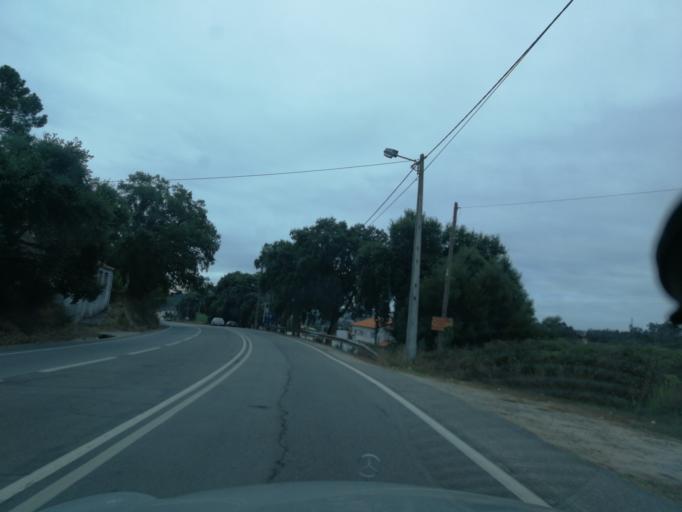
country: PT
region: Aveiro
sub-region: Agueda
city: Agueda
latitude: 40.5829
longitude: -8.4506
